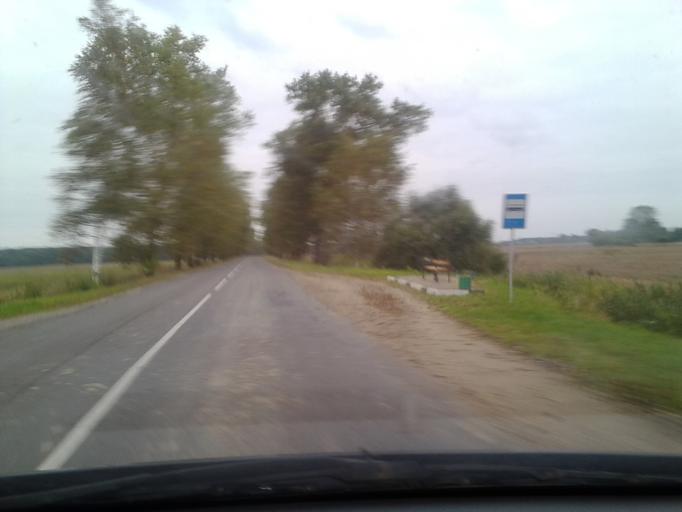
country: BY
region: Vitebsk
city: Pastavy
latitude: 55.1502
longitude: 26.9679
